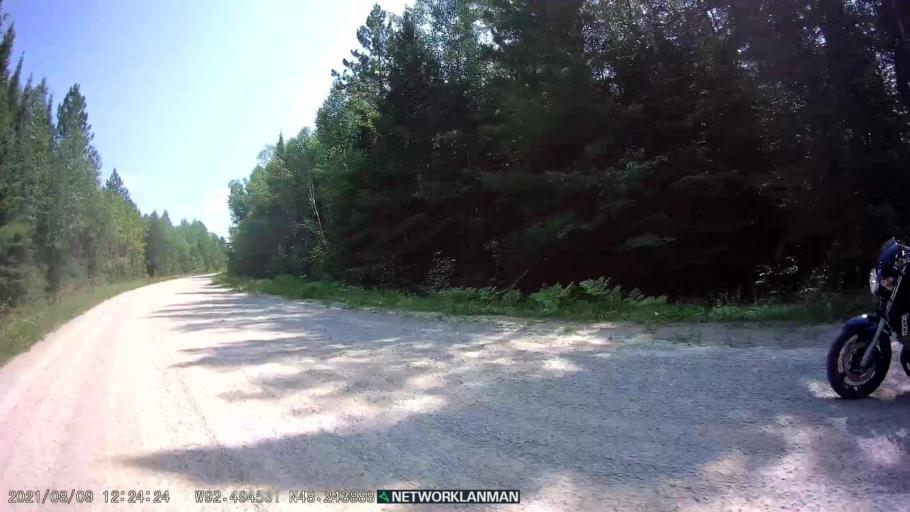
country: US
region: Minnesota
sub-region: Saint Louis County
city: Ely
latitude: 48.2439
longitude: -92.4943
